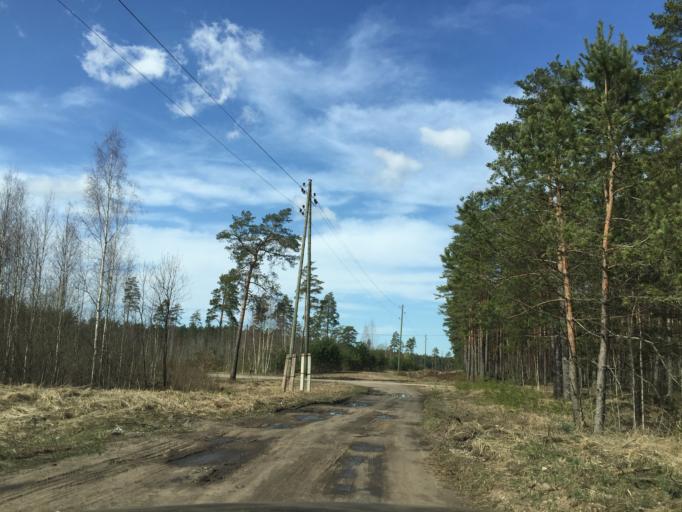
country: LV
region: Salaspils
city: Salaspils
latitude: 56.9197
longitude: 24.3991
